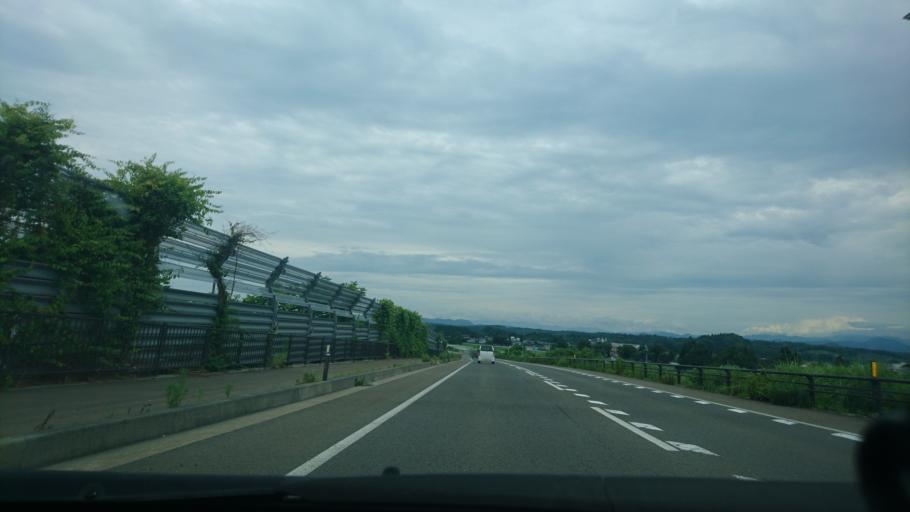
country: JP
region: Akita
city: Omagari
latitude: 39.4920
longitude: 140.4508
